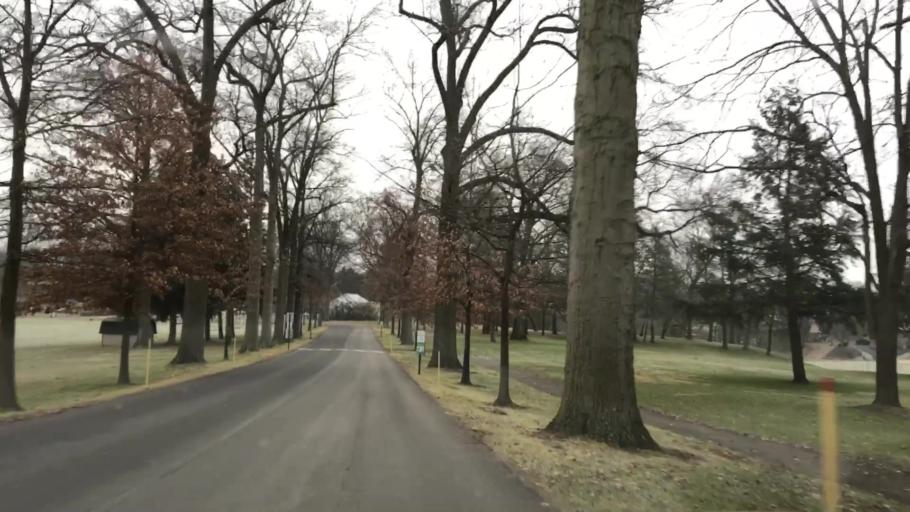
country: US
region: Pennsylvania
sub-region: Allegheny County
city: Leetsdale
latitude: 40.5741
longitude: -80.2036
